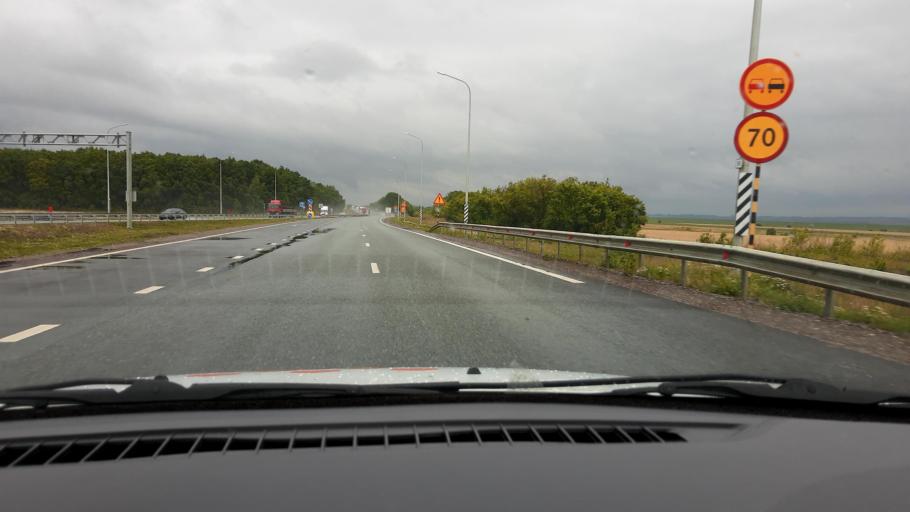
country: RU
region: Chuvashia
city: Yantikovo
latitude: 55.7957
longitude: 47.8311
